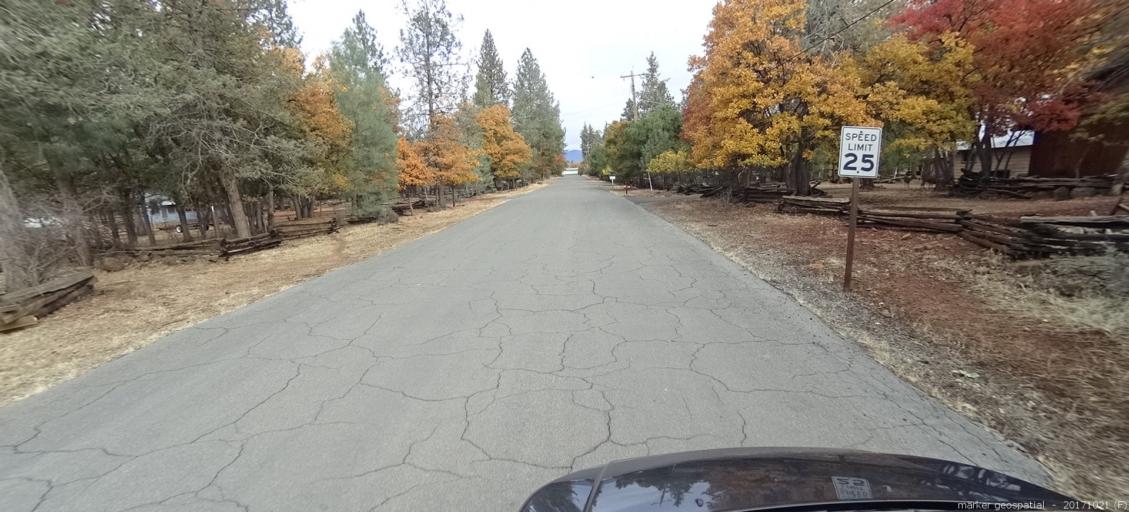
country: US
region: California
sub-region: Shasta County
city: Burney
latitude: 40.9148
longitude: -121.5546
